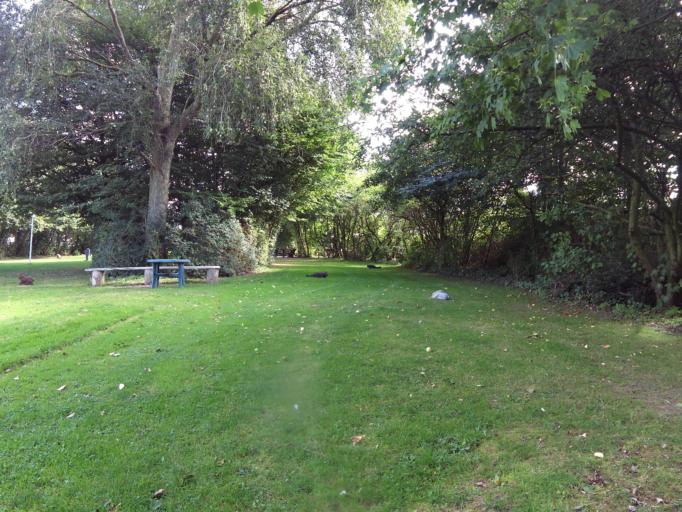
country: DK
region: South Denmark
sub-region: Sonderborg Kommune
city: Dybbol
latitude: 54.9488
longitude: 9.7021
